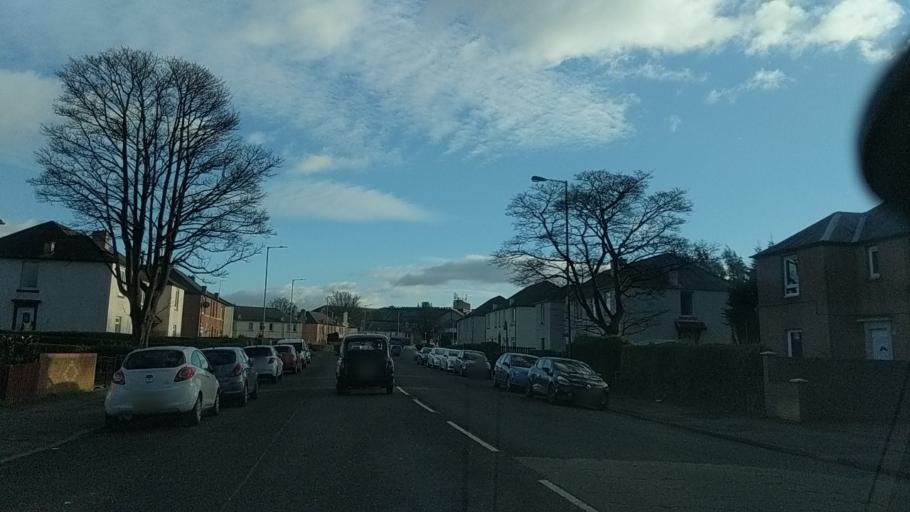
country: GB
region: Scotland
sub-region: Edinburgh
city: Colinton
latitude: 55.9323
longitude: -3.2591
